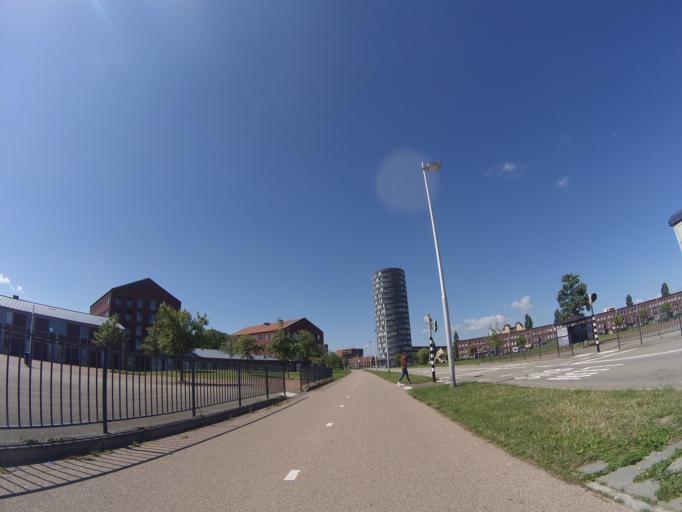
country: NL
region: Utrecht
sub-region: Stichtse Vecht
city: Maarssen
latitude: 52.0892
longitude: 5.0534
